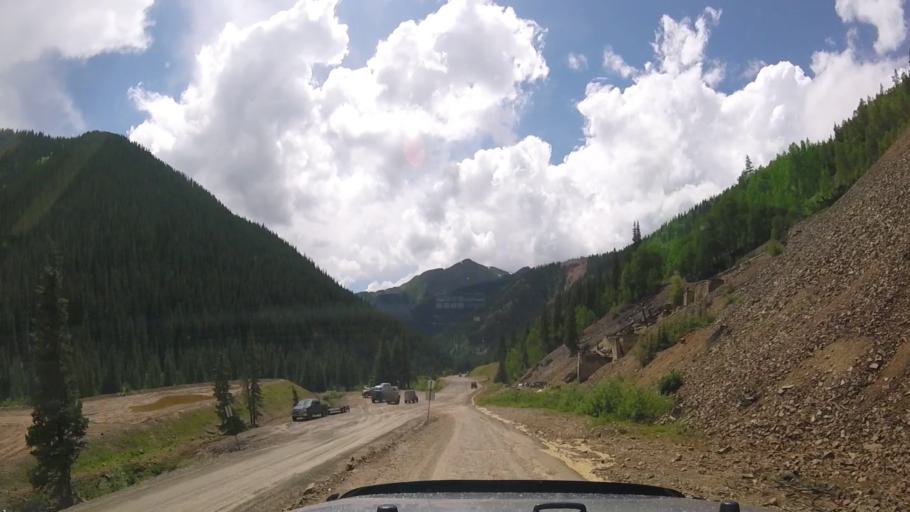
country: US
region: Colorado
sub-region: San Juan County
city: Silverton
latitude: 37.8907
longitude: -107.6512
